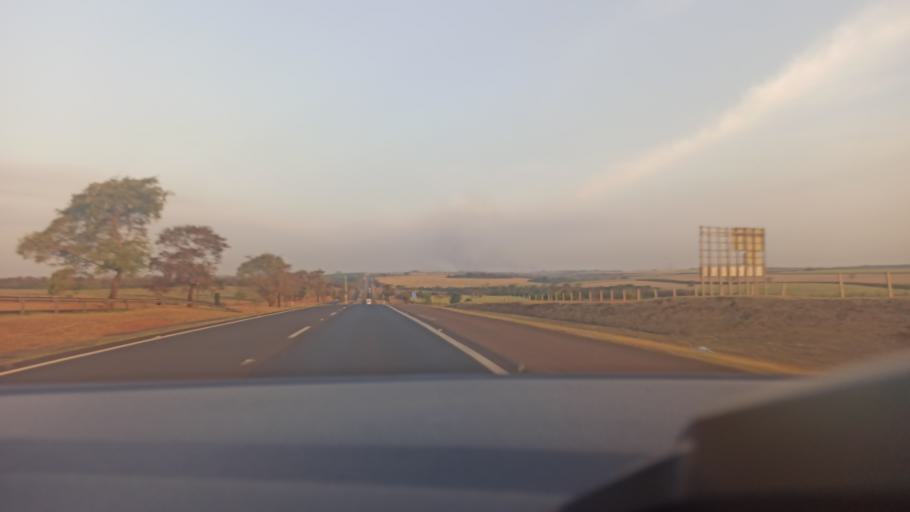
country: BR
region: Sao Paulo
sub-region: Taquaritinga
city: Taquaritinga
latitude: -21.4233
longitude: -48.6745
